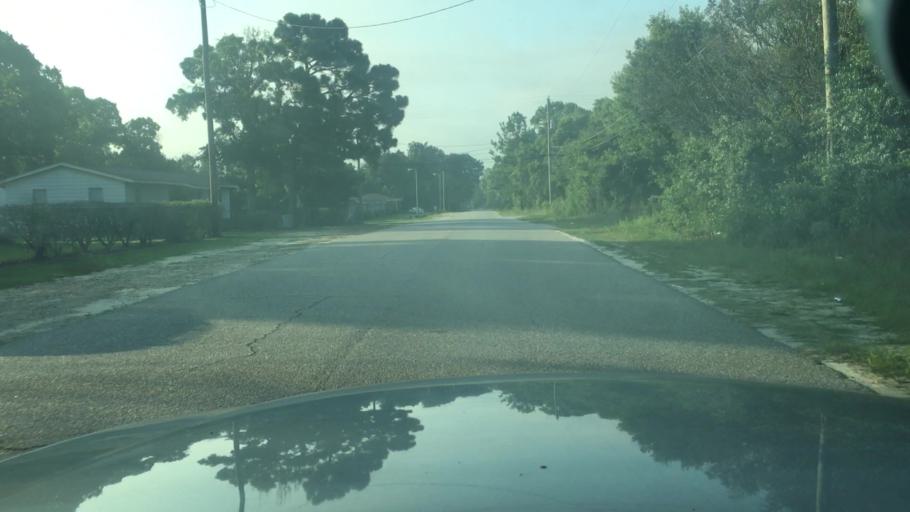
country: US
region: North Carolina
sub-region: Cumberland County
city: Spring Lake
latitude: 35.1129
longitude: -78.9372
